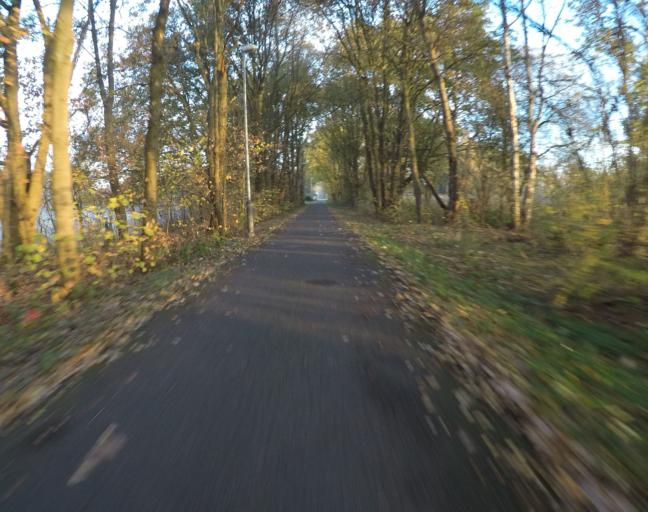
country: BE
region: Flanders
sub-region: Provincie Antwerpen
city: Hulshout
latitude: 51.0688
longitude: 4.8252
